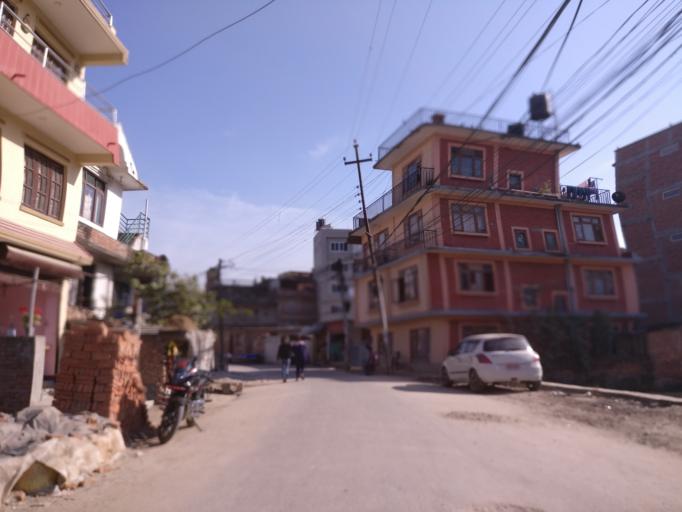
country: NP
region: Central Region
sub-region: Bagmati Zone
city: Patan
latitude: 27.6738
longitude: 85.3338
